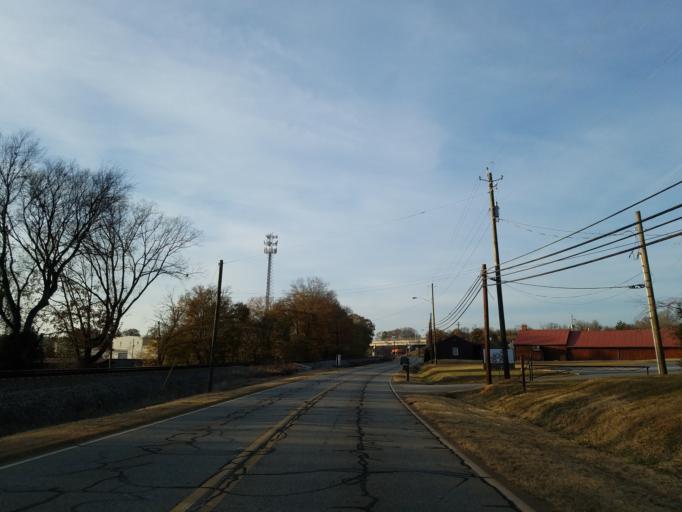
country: US
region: Georgia
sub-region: Bartow County
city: Cartersville
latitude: 34.1546
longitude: -84.7882
